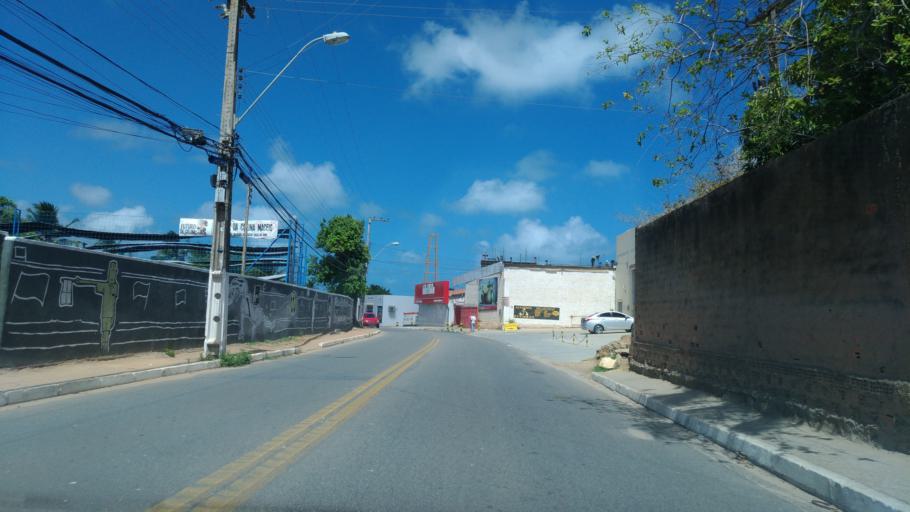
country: BR
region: Alagoas
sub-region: Maceio
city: Maceio
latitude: -9.6196
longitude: -35.7078
